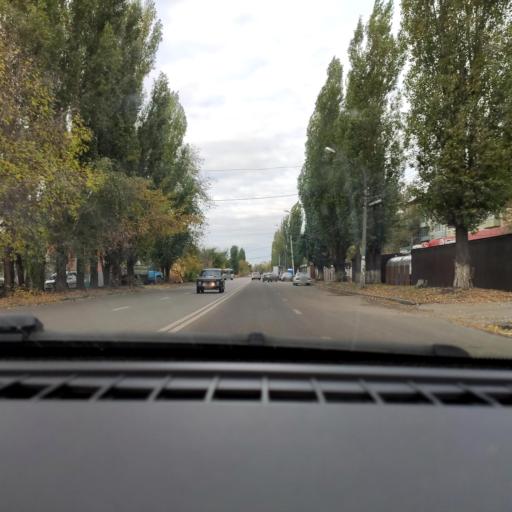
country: RU
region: Voronezj
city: Maslovka
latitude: 51.6325
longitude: 39.2701
